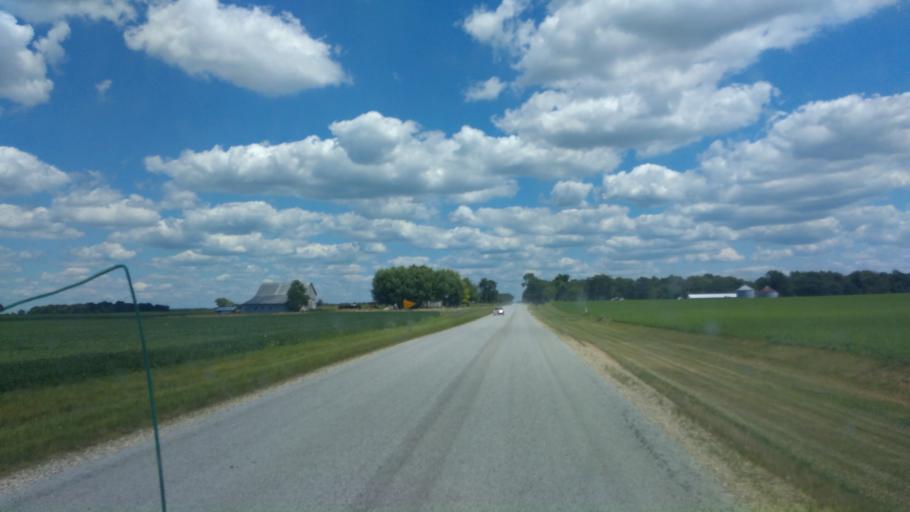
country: US
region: Indiana
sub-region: Adams County
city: Geneva
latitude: 40.5908
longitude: -85.0310
